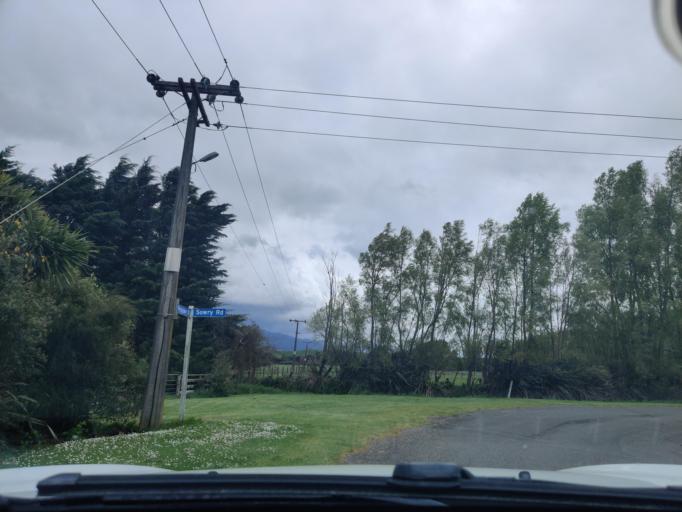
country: NZ
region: Manawatu-Wanganui
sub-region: Palmerston North City
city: Palmerston North
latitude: -40.3296
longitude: 175.8665
